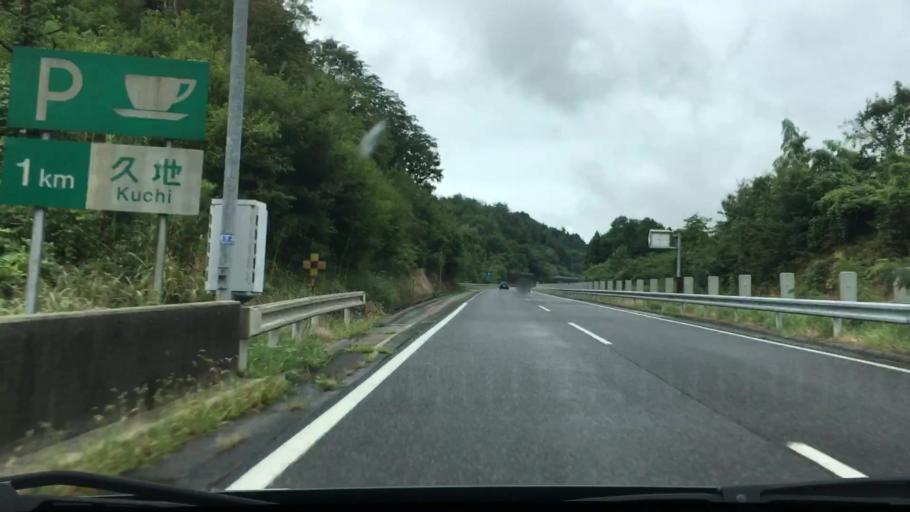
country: JP
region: Hiroshima
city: Hiroshima-shi
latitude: 34.5036
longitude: 132.4088
